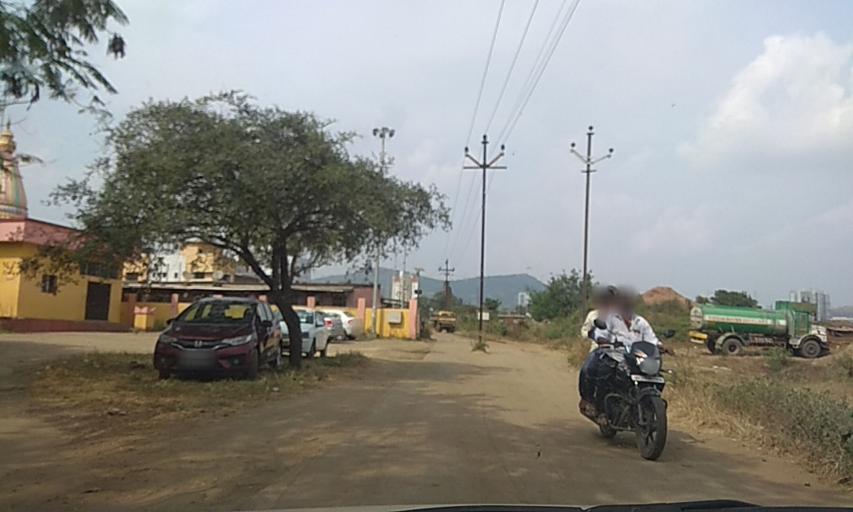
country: IN
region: Maharashtra
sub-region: Pune Division
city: Pimpri
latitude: 18.5822
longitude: 73.7066
